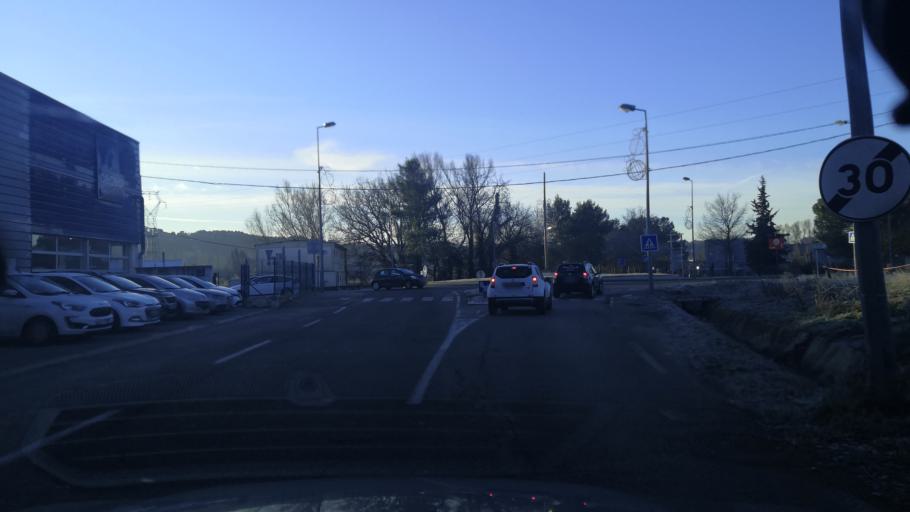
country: FR
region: Provence-Alpes-Cote d'Azur
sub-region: Departement des Bouches-du-Rhone
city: Aix-en-Provence
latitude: 43.5115
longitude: 5.4100
